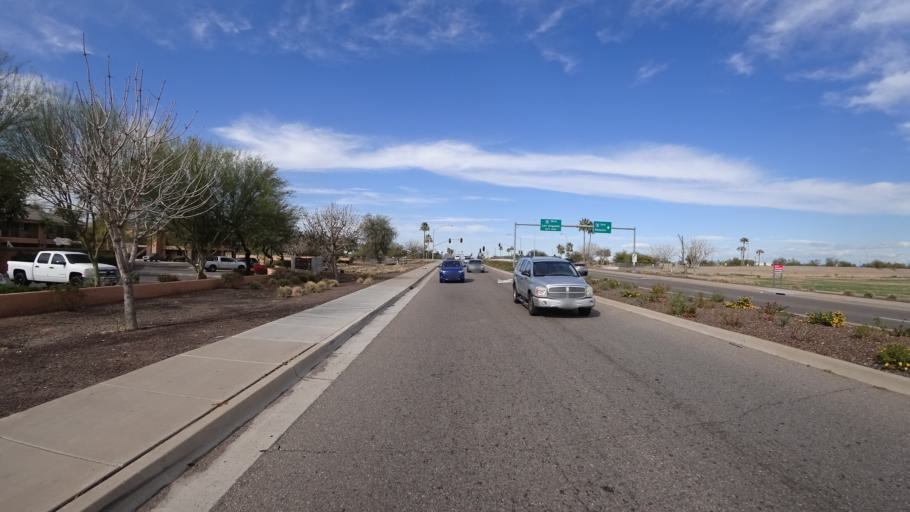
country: US
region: Arizona
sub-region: Maricopa County
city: Tolleson
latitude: 33.4606
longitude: -112.2553
